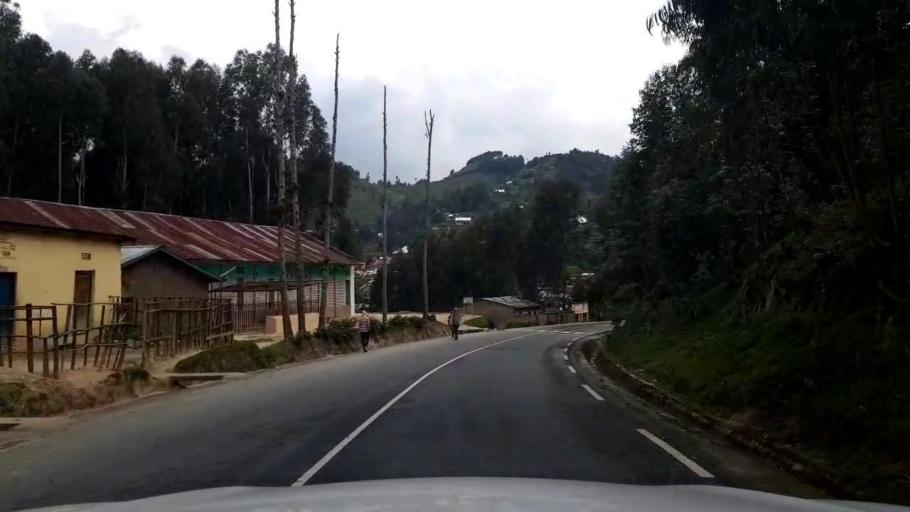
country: RW
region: Northern Province
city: Musanze
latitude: -1.6839
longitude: 29.5168
